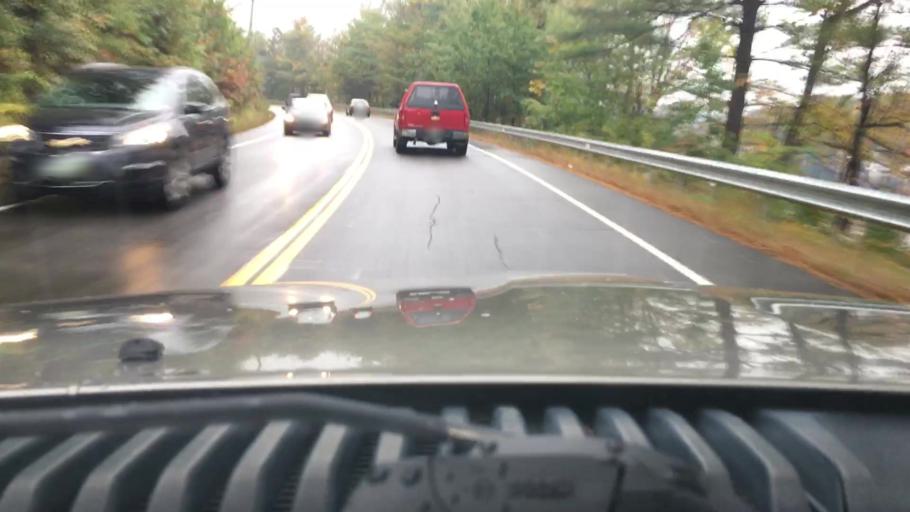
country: US
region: New Hampshire
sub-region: Hillsborough County
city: Manchester
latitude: 43.0213
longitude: -71.4808
